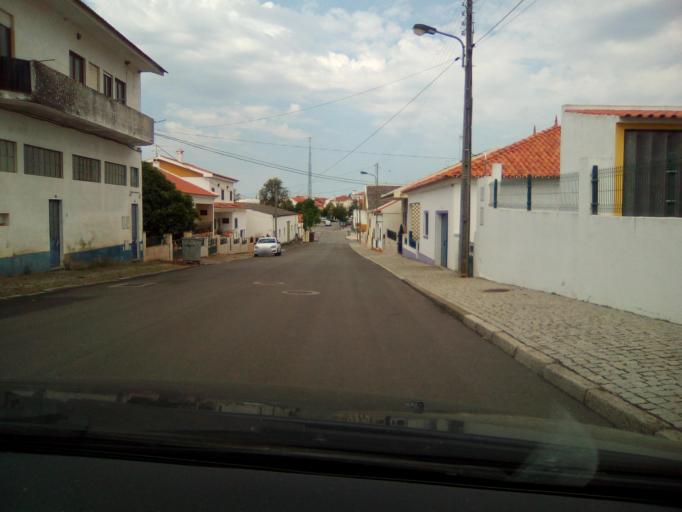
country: PT
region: Portalegre
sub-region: Avis
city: Avis
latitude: 39.0519
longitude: -7.8863
